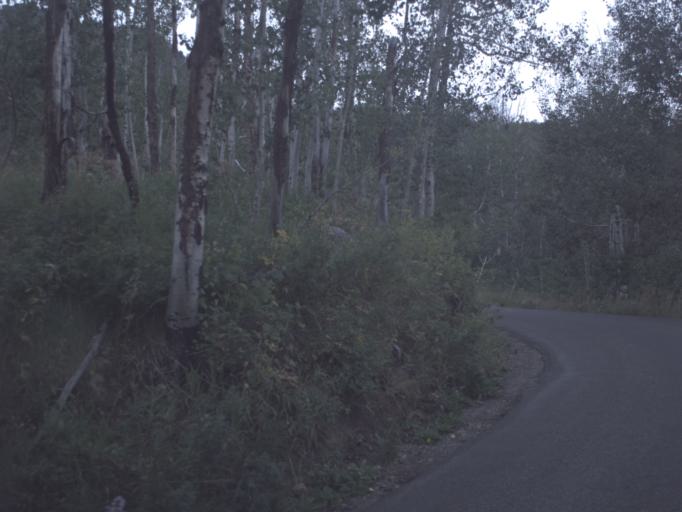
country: US
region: Utah
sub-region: Utah County
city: Lindon
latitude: 40.4279
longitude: -111.6097
